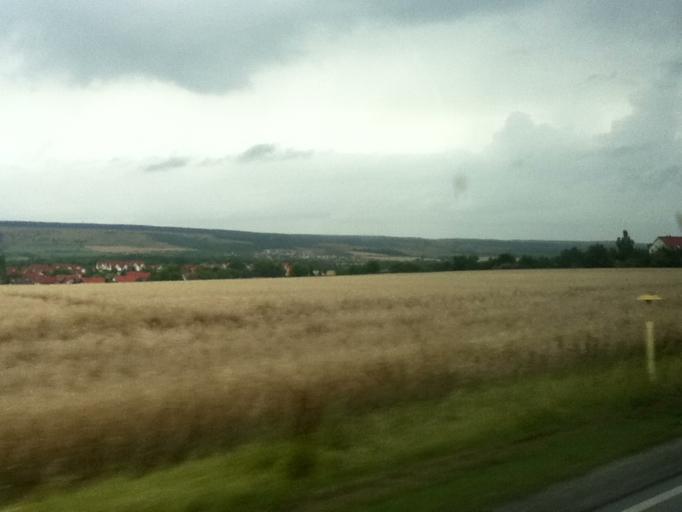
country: DE
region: Thuringia
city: Hopfgarten
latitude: 50.9693
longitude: 11.2628
